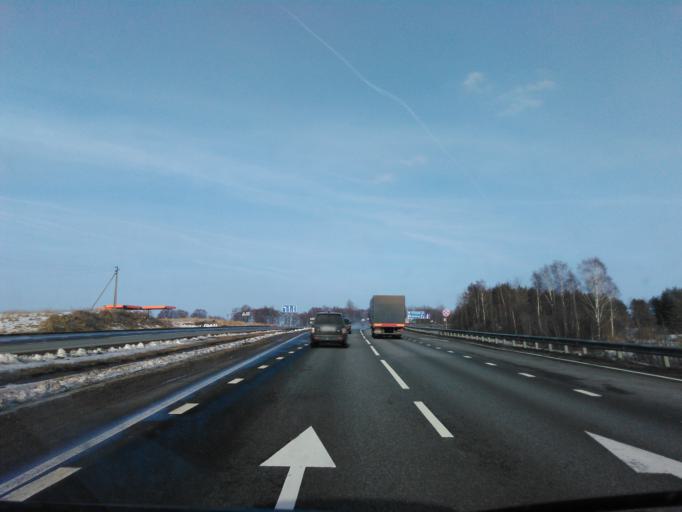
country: RU
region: Smolensk
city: Vyaz'ma
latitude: 55.2089
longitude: 34.1557
